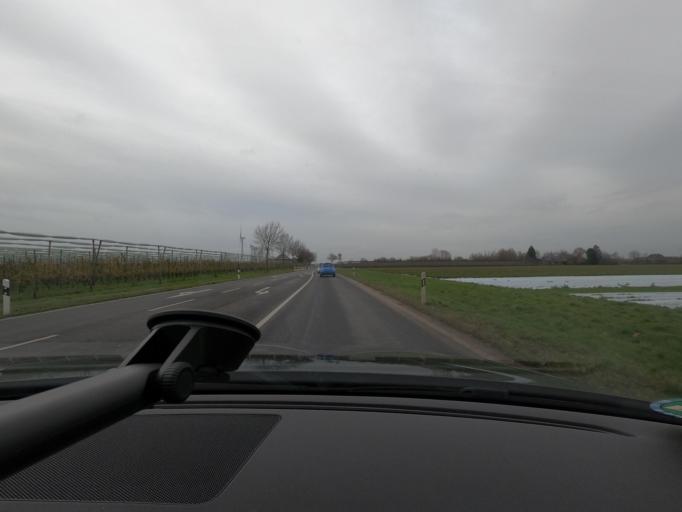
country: DE
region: North Rhine-Westphalia
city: Tonisvorst
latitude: 51.3384
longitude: 6.4957
